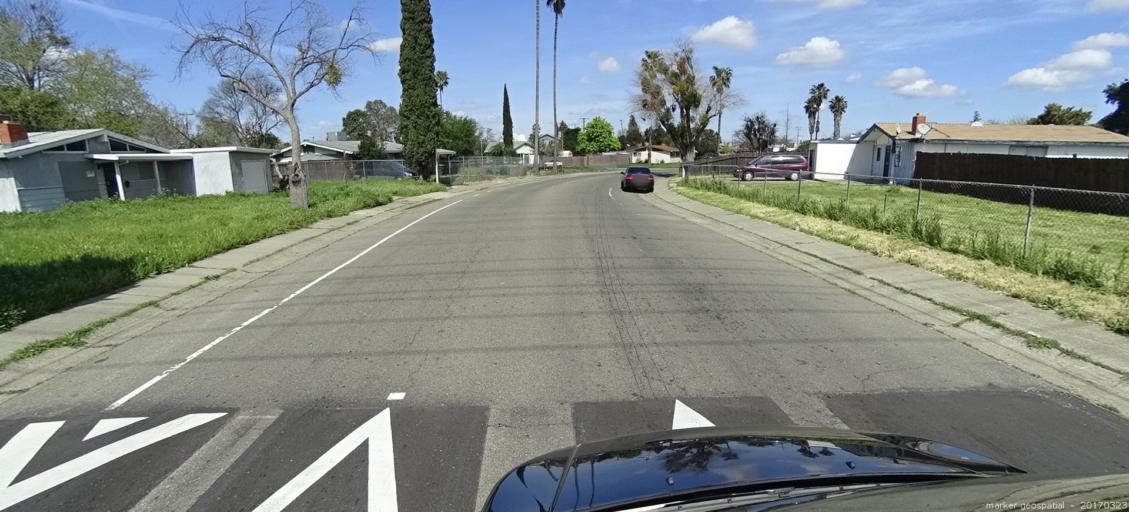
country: US
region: California
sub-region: Sacramento County
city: Florin
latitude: 38.5086
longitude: -121.4166
